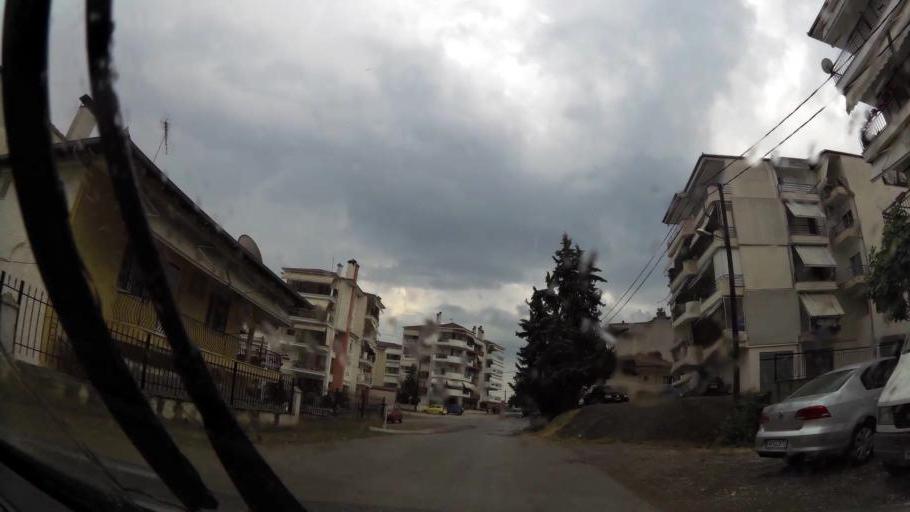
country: GR
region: Central Macedonia
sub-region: Nomos Imathias
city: Veroia
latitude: 40.5260
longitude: 22.1947
